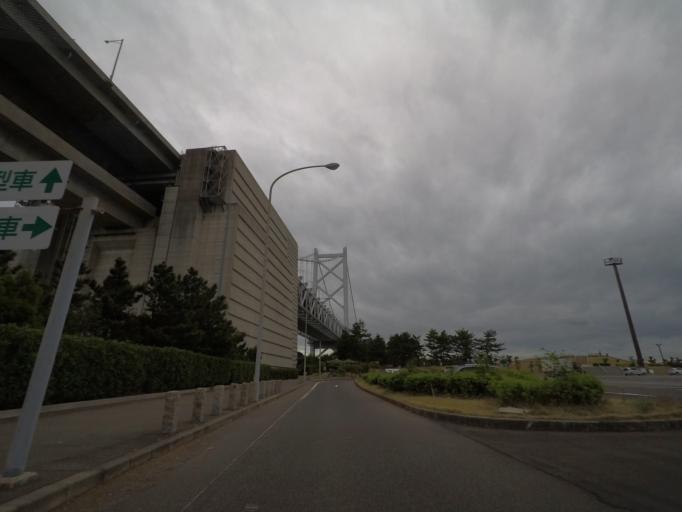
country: JP
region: Kagawa
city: Sakaidecho
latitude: 34.3862
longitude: 133.8173
